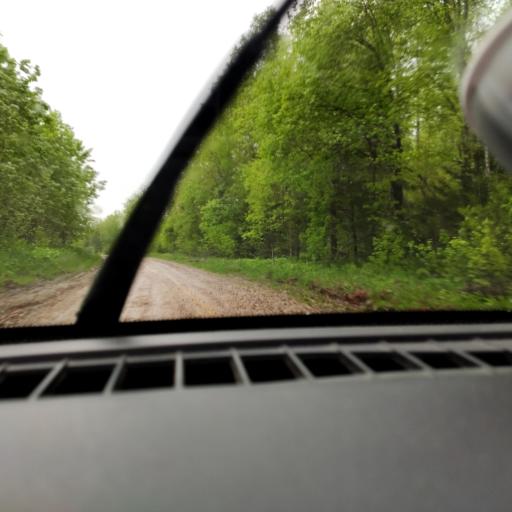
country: RU
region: Perm
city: Polazna
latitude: 58.2949
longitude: 56.1435
